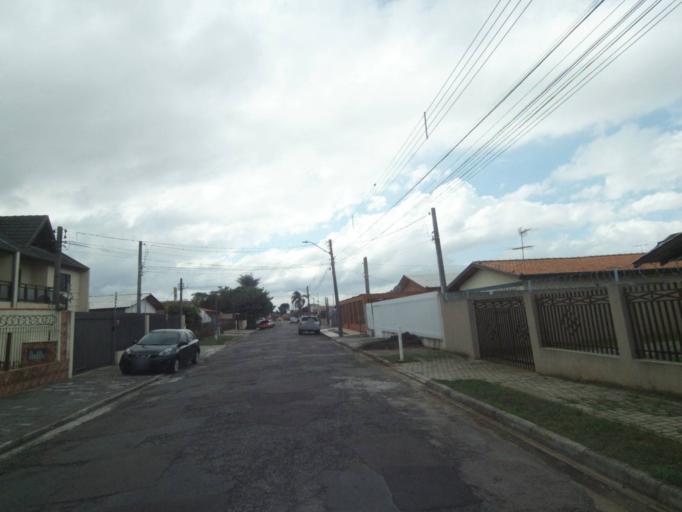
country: BR
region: Parana
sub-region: Pinhais
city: Pinhais
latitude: -25.4522
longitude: -49.2092
